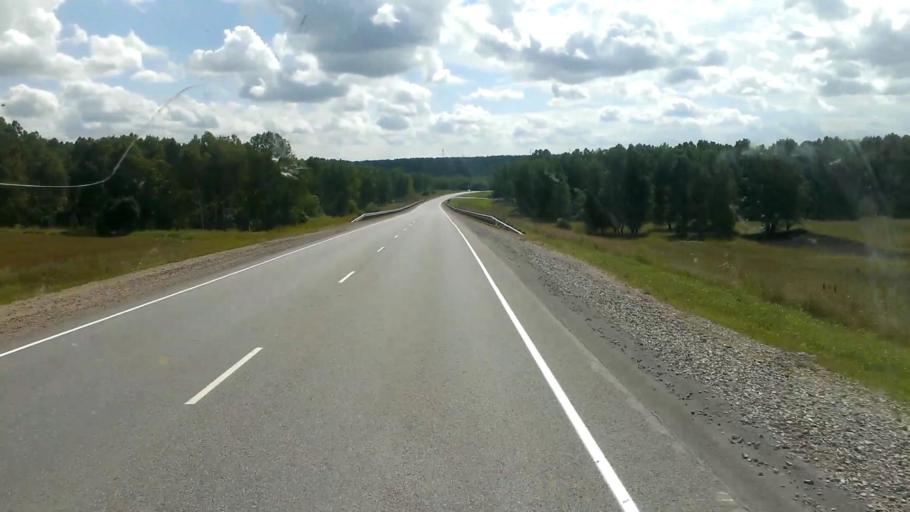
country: RU
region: Altai Krai
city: Troitskoye
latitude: 52.9425
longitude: 84.7787
